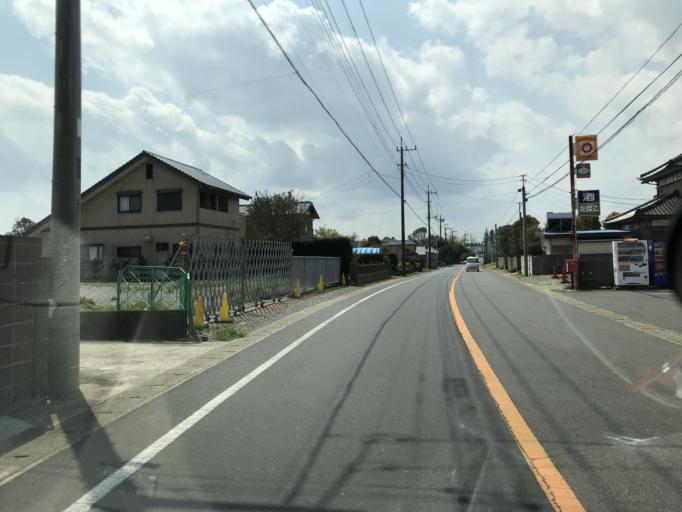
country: JP
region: Chiba
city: Omigawa
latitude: 35.8639
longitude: 140.5640
